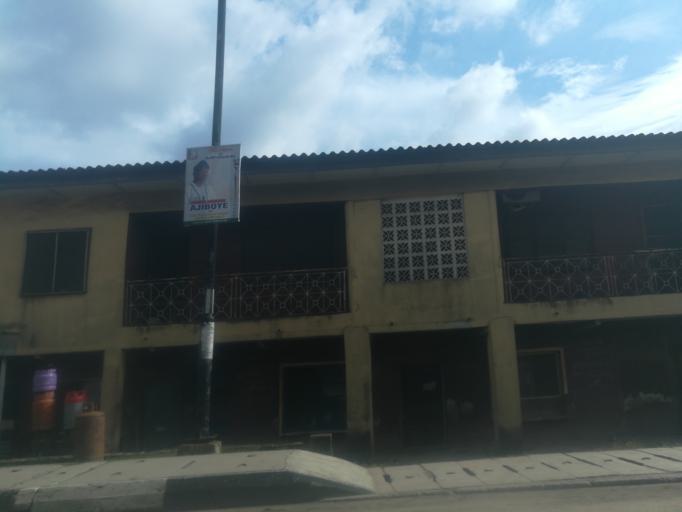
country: NG
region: Lagos
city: Somolu
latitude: 6.5438
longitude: 3.3751
